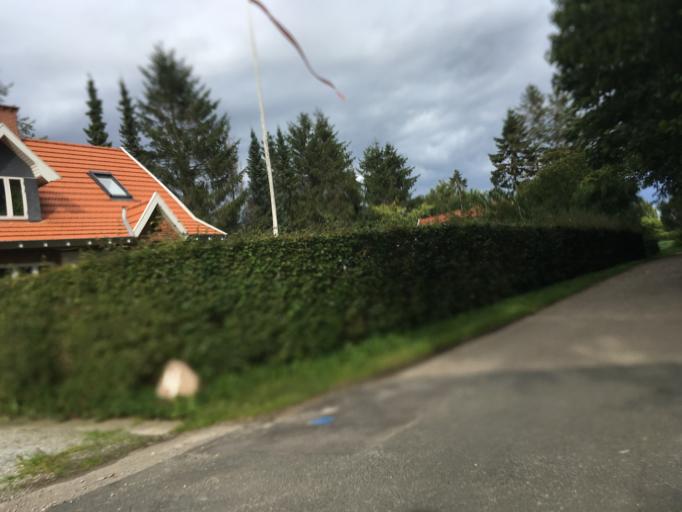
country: DK
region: Capital Region
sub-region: Hillerod Kommune
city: Hillerod
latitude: 55.9307
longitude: 12.2749
